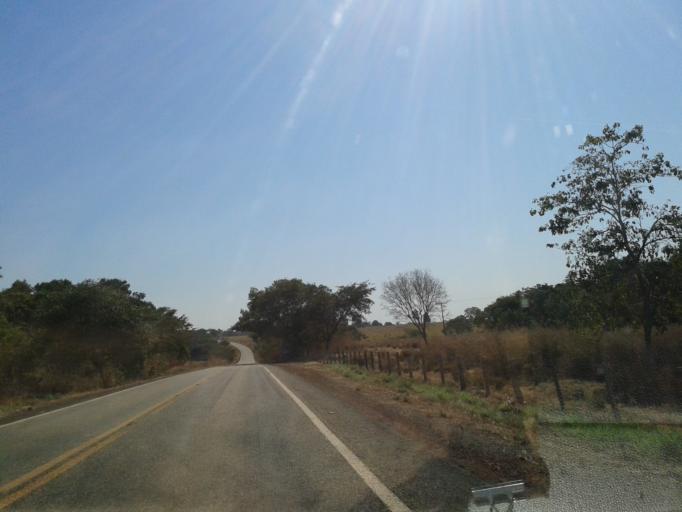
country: BR
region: Goias
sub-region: Mozarlandia
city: Mozarlandia
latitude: -14.3133
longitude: -50.4068
